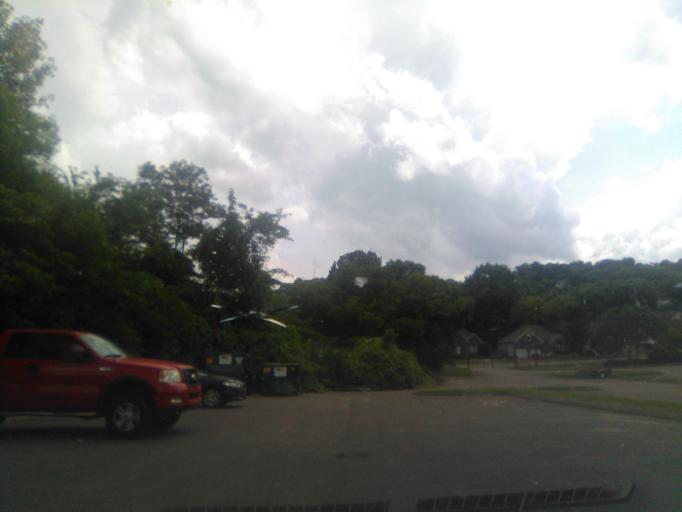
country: US
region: Tennessee
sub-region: Davidson County
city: Belle Meade
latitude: 36.0838
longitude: -86.8879
